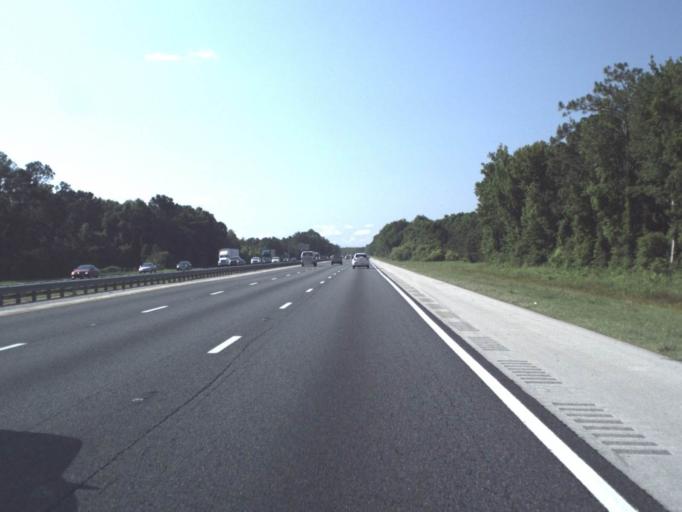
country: US
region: Florida
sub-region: Saint Johns County
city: Villano Beach
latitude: 29.9735
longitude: -81.4544
